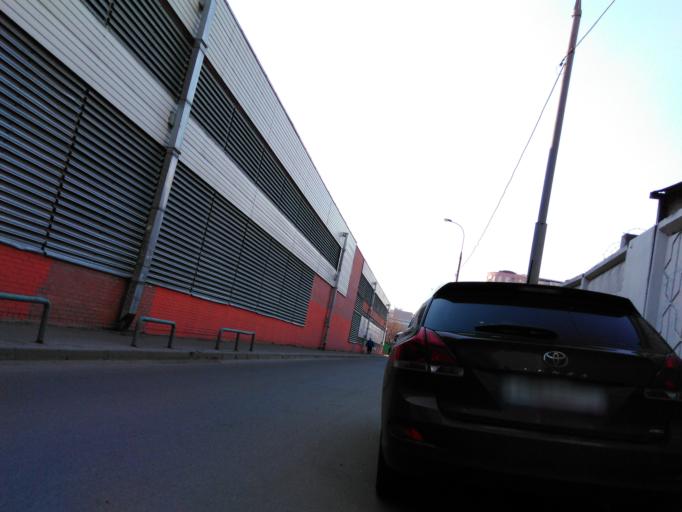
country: RU
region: Moscow
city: Ramenki
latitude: 55.6934
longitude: 37.5027
